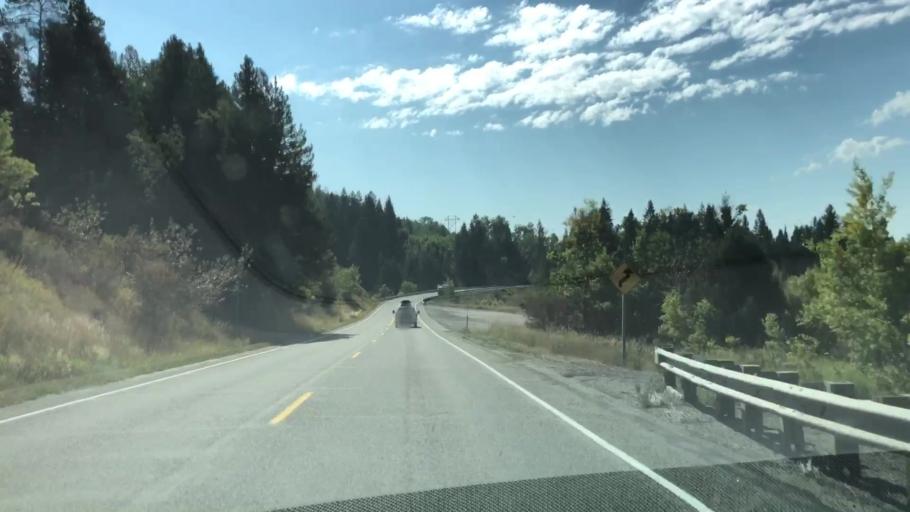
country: US
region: Idaho
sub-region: Teton County
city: Victor
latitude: 43.3015
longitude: -111.1316
